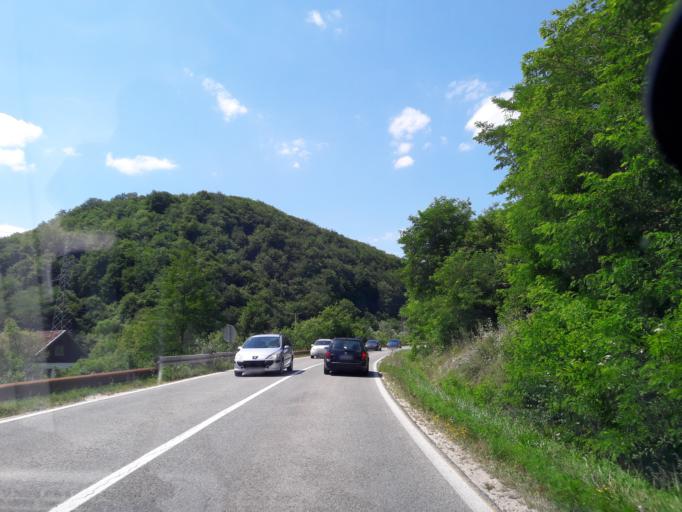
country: BA
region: Republika Srpska
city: Mrkonjic Grad
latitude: 44.3773
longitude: 17.1299
